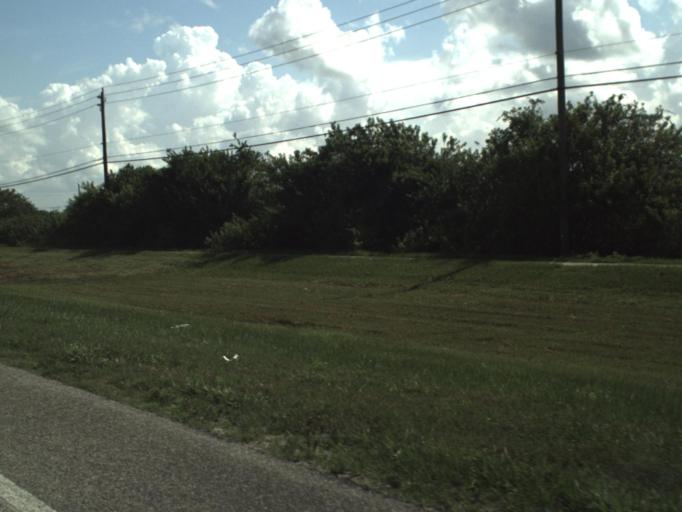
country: US
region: Florida
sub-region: Palm Beach County
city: Villages of Oriole
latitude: 26.5174
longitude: -80.2054
